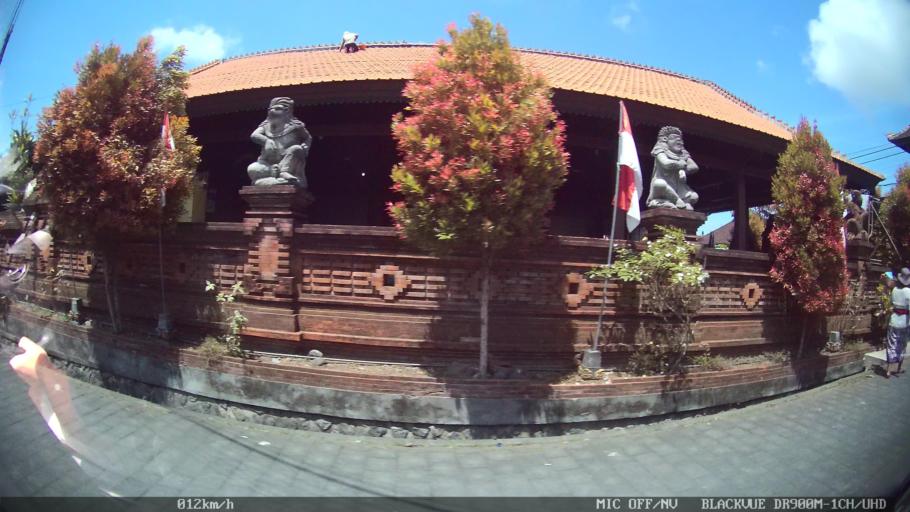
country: ID
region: Bali
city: Banjar Paangkelod
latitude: -8.6123
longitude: 115.2551
